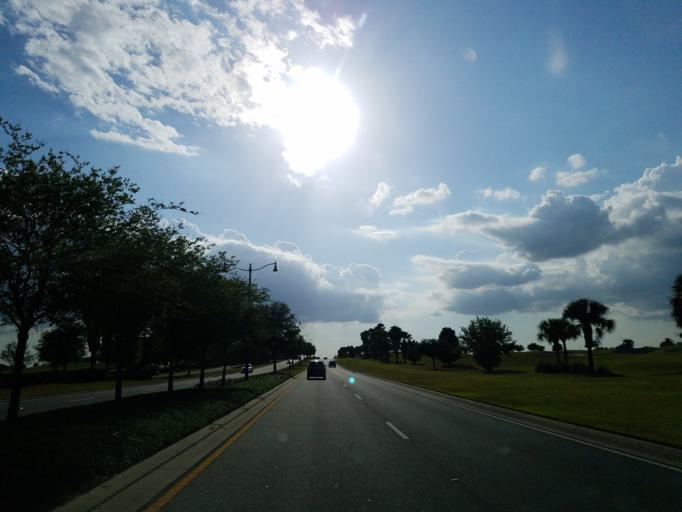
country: US
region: Florida
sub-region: Sumter County
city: Wildwood
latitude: 28.8654
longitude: -81.9769
